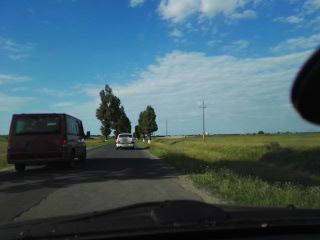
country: RO
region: Giurgiu
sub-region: Comuna Comana
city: Gradistea
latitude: 44.2001
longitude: 26.1427
